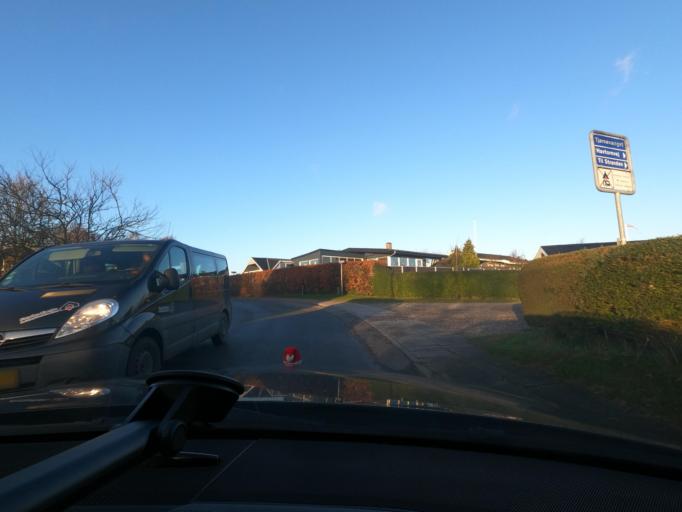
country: DK
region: South Denmark
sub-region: Sonderborg Kommune
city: Broager
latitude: 54.9012
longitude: 9.7020
